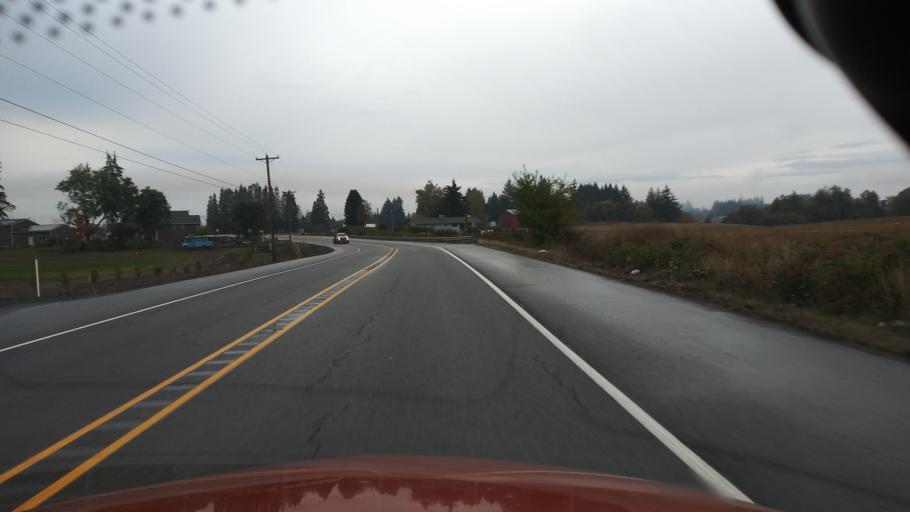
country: US
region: Oregon
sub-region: Washington County
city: Cornelius
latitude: 45.5443
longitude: -123.0595
